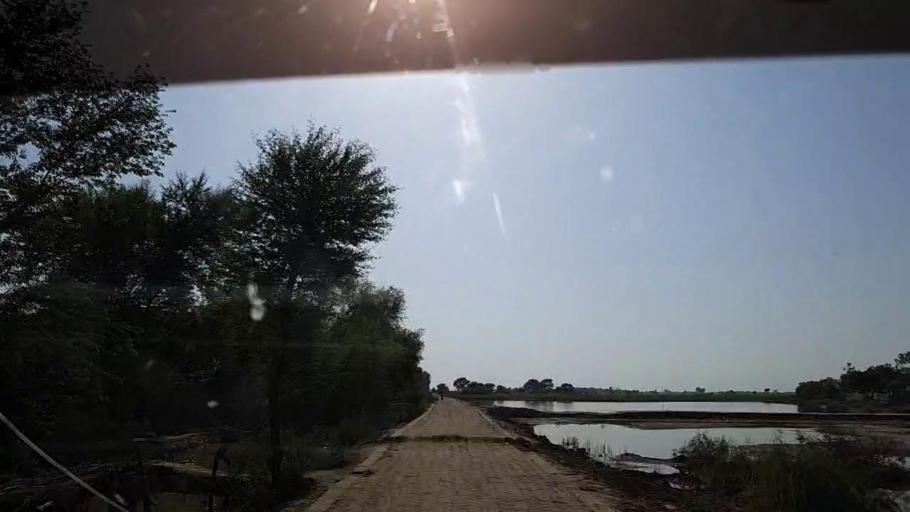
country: PK
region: Sindh
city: Tangwani
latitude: 28.2151
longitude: 68.9685
